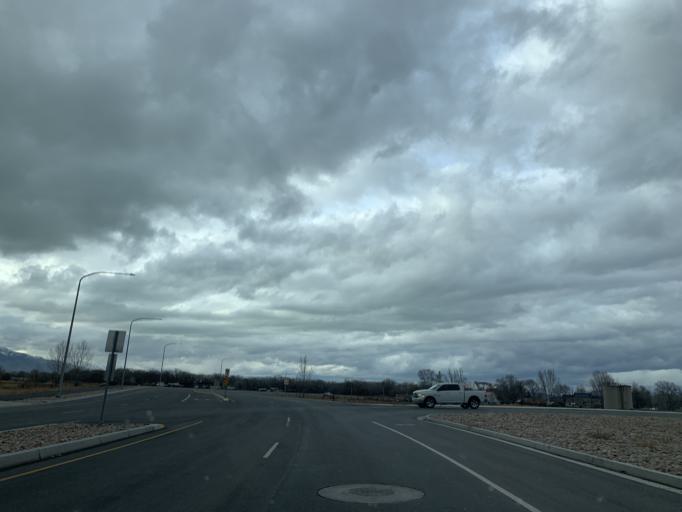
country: US
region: Utah
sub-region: Utah County
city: Provo
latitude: 40.2308
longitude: -111.7134
